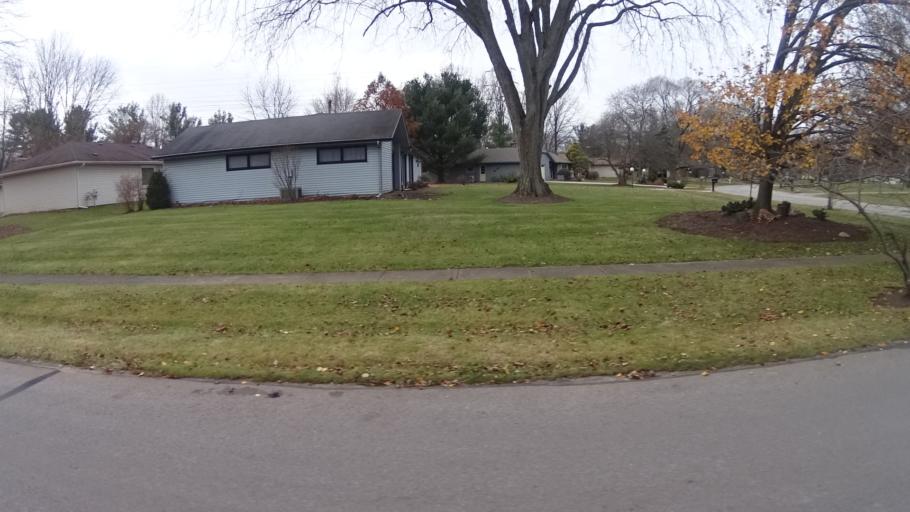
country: US
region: Ohio
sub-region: Lorain County
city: North Ridgeville
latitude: 41.3980
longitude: -81.9726
